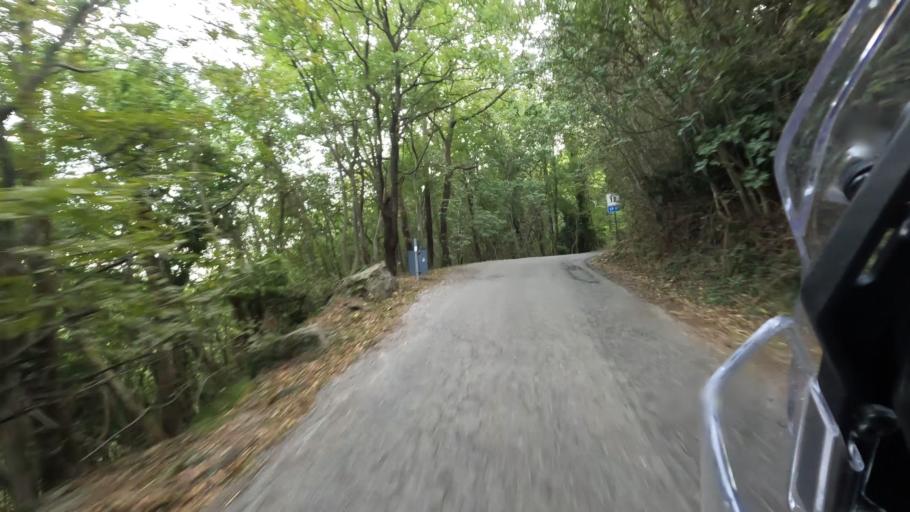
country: IT
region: Liguria
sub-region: Provincia di Savona
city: San Giovanni
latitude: 44.3969
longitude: 8.5343
